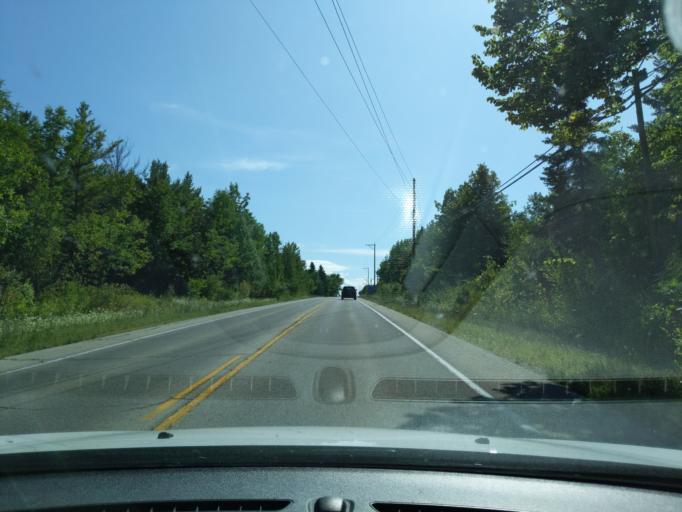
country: US
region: Wisconsin
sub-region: Door County
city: Sturgeon Bay
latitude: 45.2175
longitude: -87.1097
